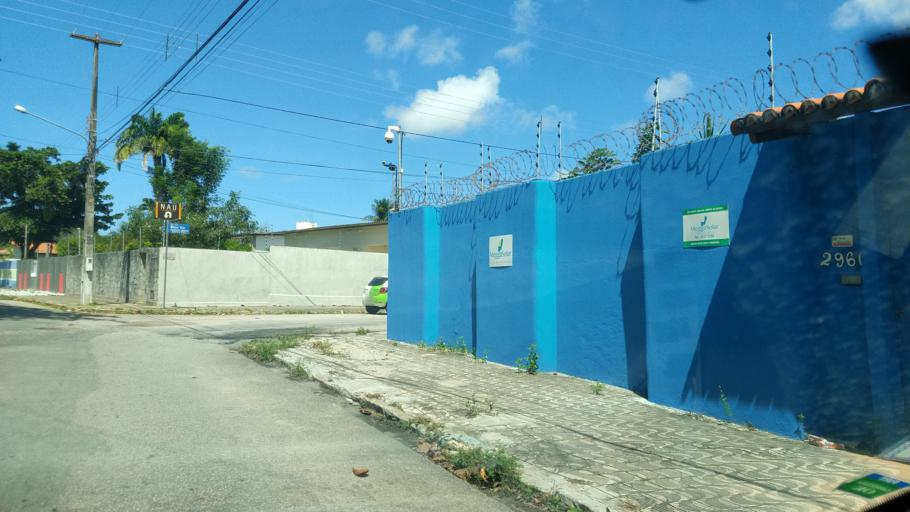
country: BR
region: Rio Grande do Norte
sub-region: Natal
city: Natal
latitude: -5.8483
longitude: -35.1996
